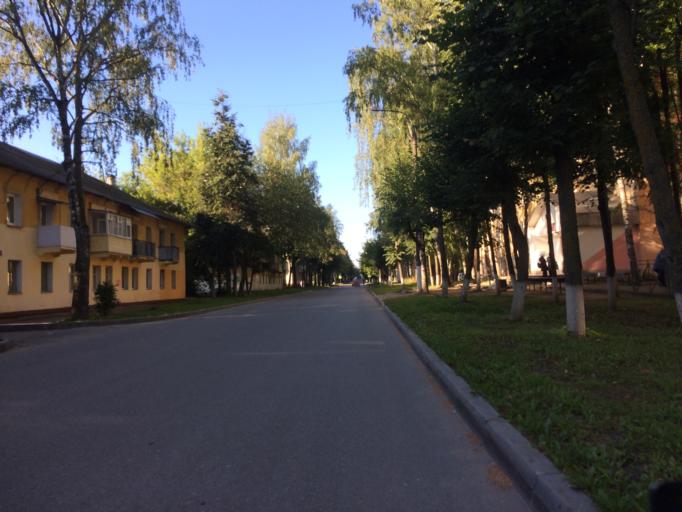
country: RU
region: Mariy-El
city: Yoshkar-Ola
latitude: 56.6423
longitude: 47.8850
